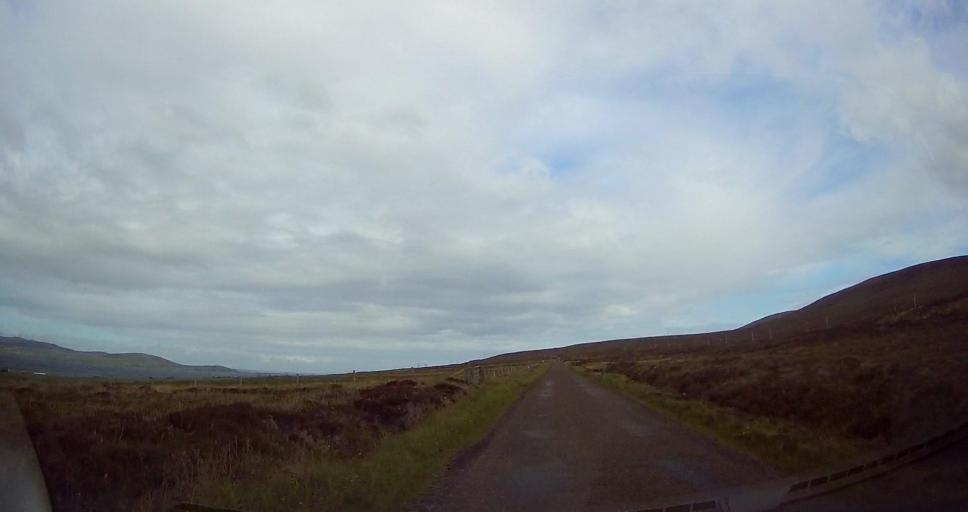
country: GB
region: Scotland
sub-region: Orkney Islands
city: Stromness
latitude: 58.9033
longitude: -3.3017
